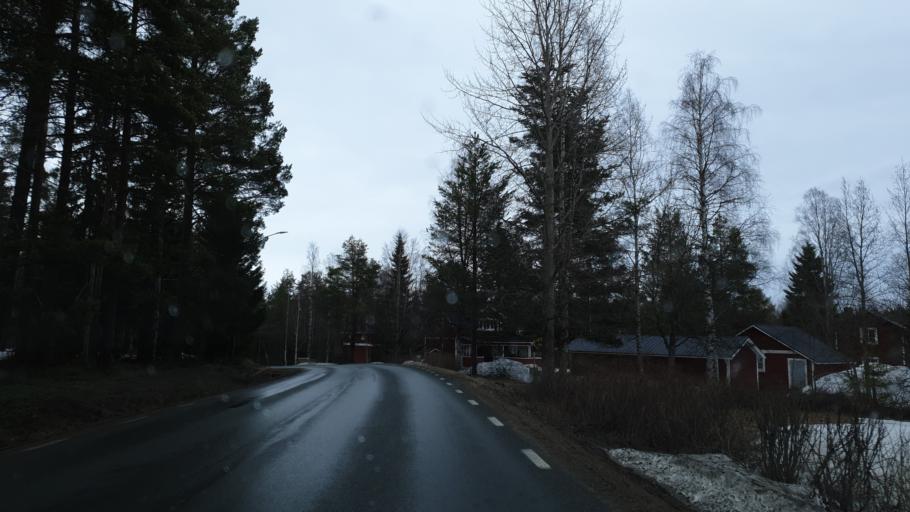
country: SE
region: Vaesterbotten
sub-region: Skelleftea Kommun
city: Kage
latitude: 64.8263
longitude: 20.9854
